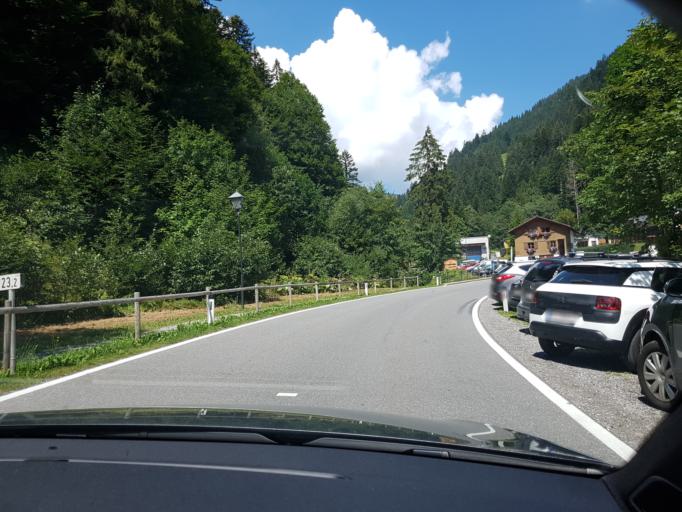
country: AT
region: Vorarlberg
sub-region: Politischer Bezirk Bregenz
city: Damuels
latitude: 47.2545
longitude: 9.9141
